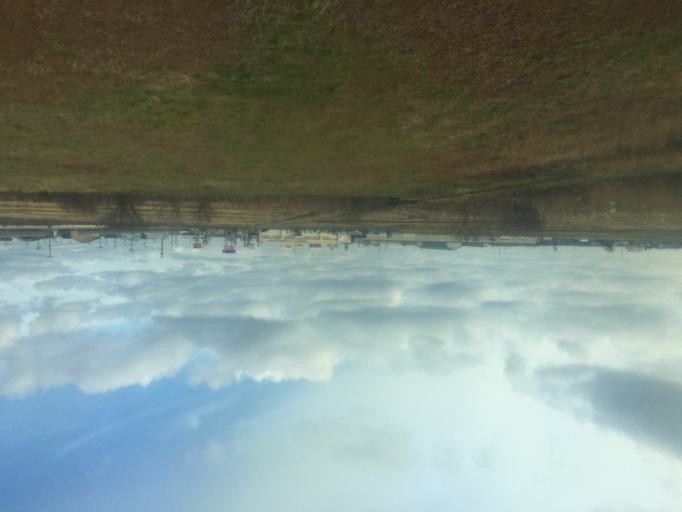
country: JP
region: Akita
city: Noshiromachi
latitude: 40.1833
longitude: 140.0591
